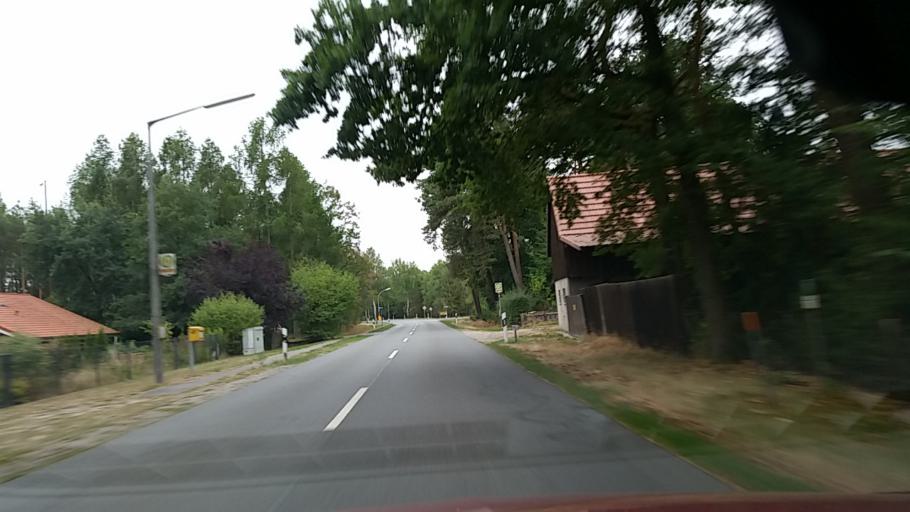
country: DE
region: Lower Saxony
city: Schoneworde
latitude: 52.6303
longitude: 10.6908
